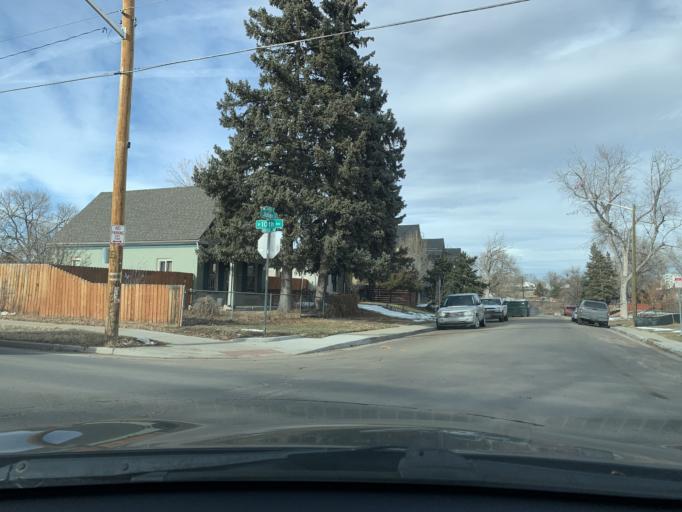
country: US
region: Colorado
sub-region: Jefferson County
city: Edgewater
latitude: 39.7329
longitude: -105.0310
